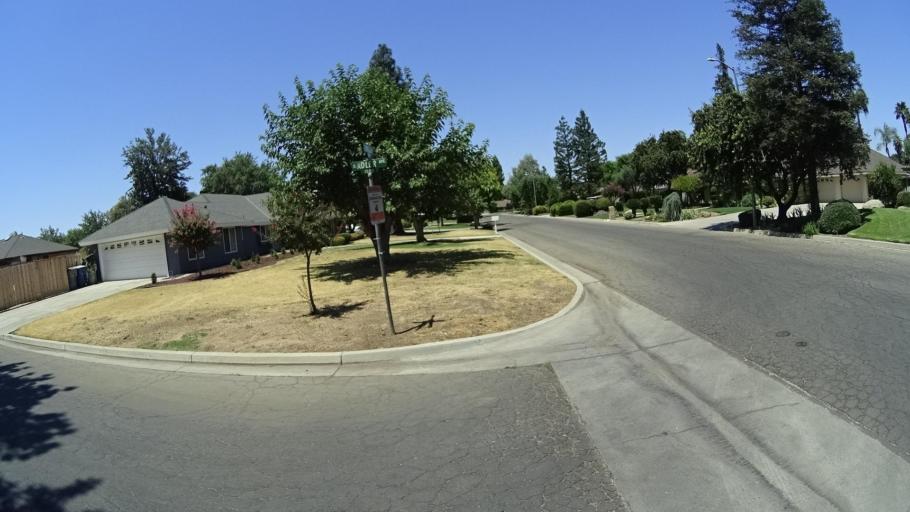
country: US
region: California
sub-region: Fresno County
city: Sunnyside
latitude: 36.7277
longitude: -119.7244
